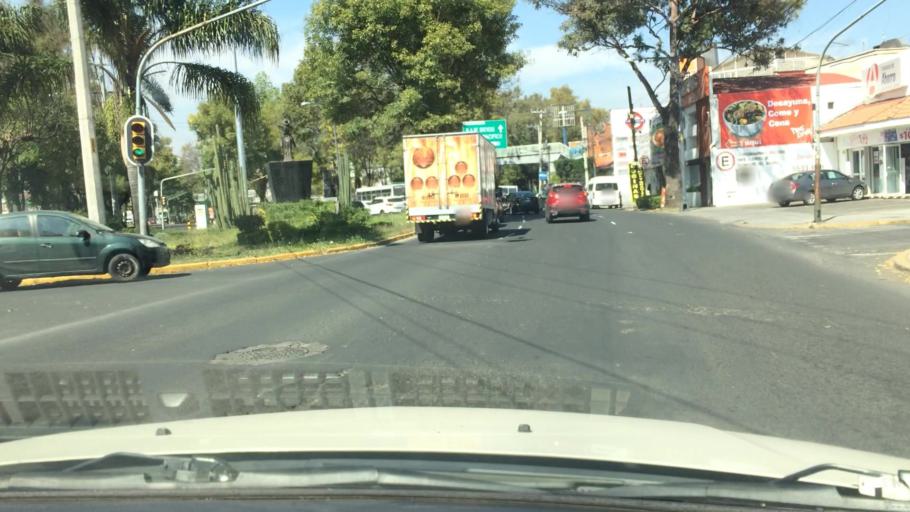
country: MX
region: Mexico City
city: Coyoacan
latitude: 19.3334
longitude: -99.1459
